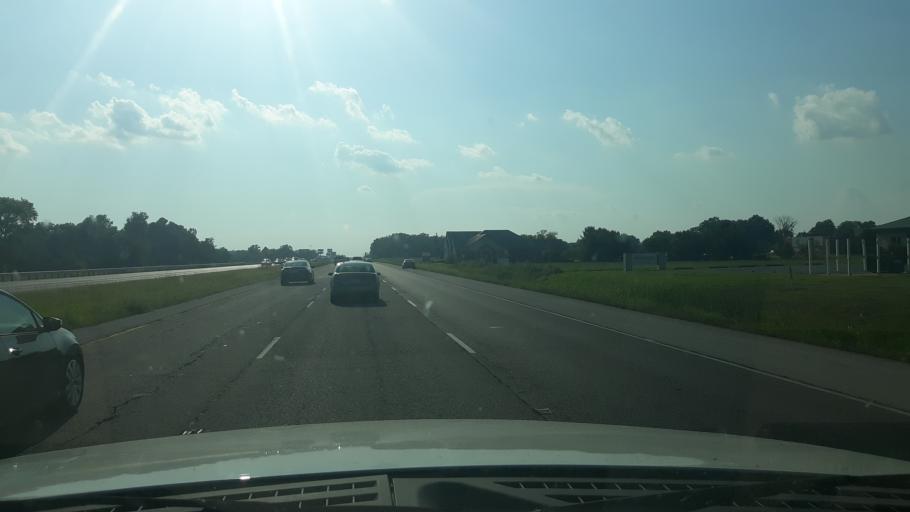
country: US
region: Illinois
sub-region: Williamson County
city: Energy
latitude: 37.7452
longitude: -89.0278
